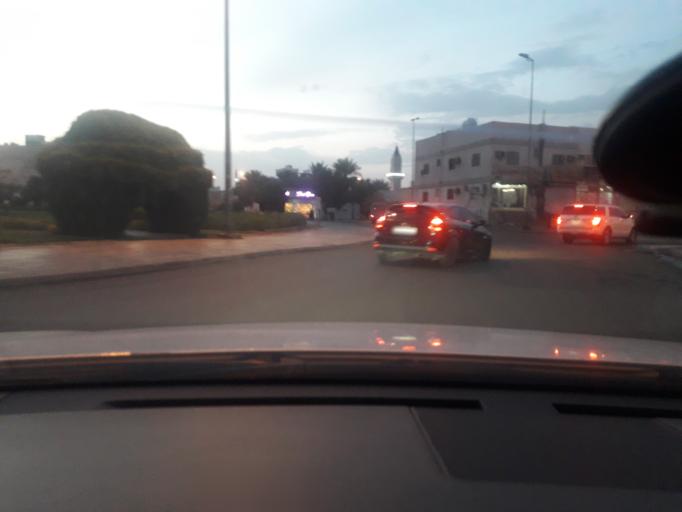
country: SA
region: Al Madinah al Munawwarah
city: Sultanah
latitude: 24.4931
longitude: 39.5863
